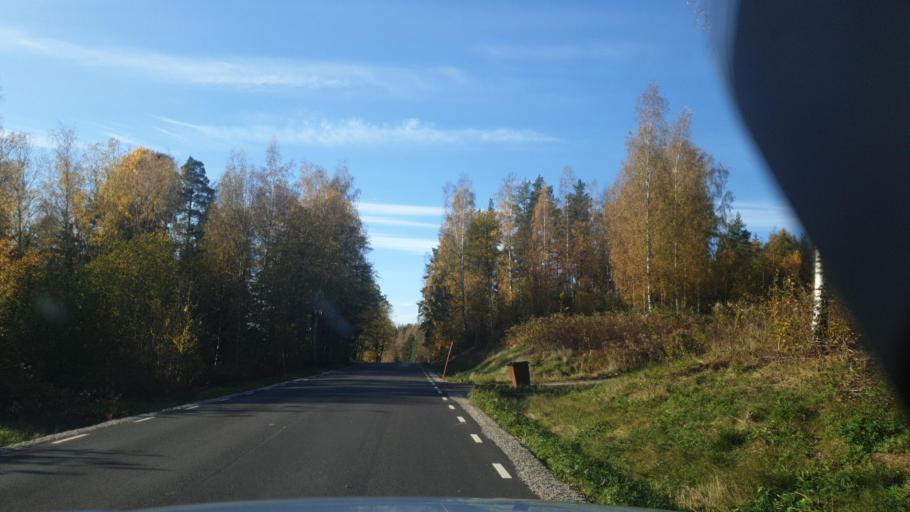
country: SE
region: Vaermland
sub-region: Arvika Kommun
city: Arvika
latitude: 59.6637
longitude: 12.6902
